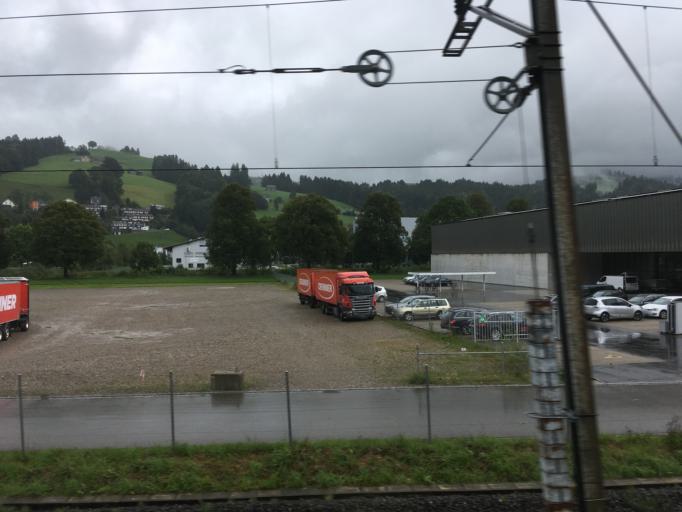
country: CH
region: Saint Gallen
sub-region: Wahlkreis Toggenburg
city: Wattwil
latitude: 47.2921
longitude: 9.0903
